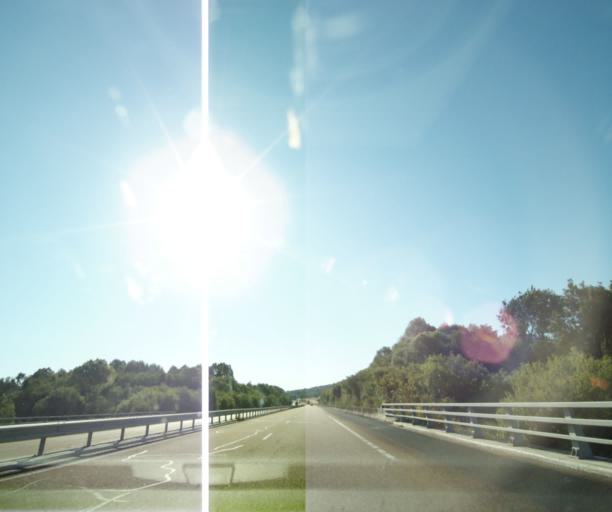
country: FR
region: Champagne-Ardenne
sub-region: Departement de l'Aube
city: Estissac
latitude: 48.2733
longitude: 3.8559
